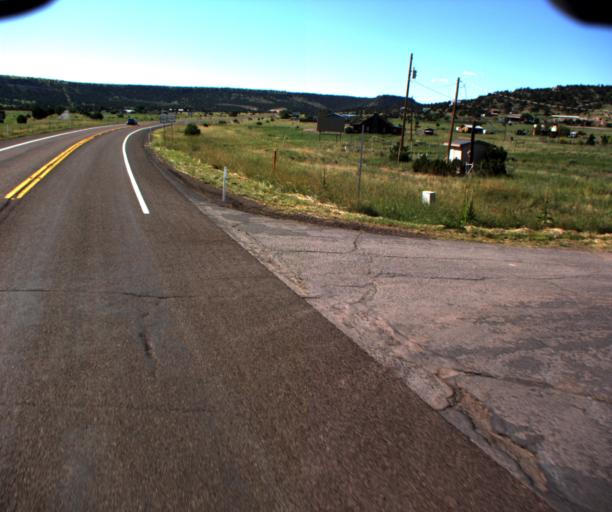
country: US
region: Arizona
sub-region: Apache County
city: Eagar
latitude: 34.1075
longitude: -109.2483
